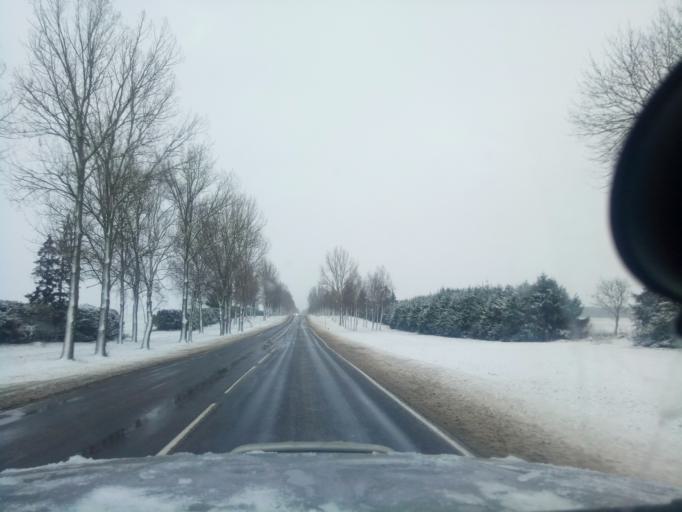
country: BY
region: Minsk
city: Haradzyeya
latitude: 53.3521
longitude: 26.5168
